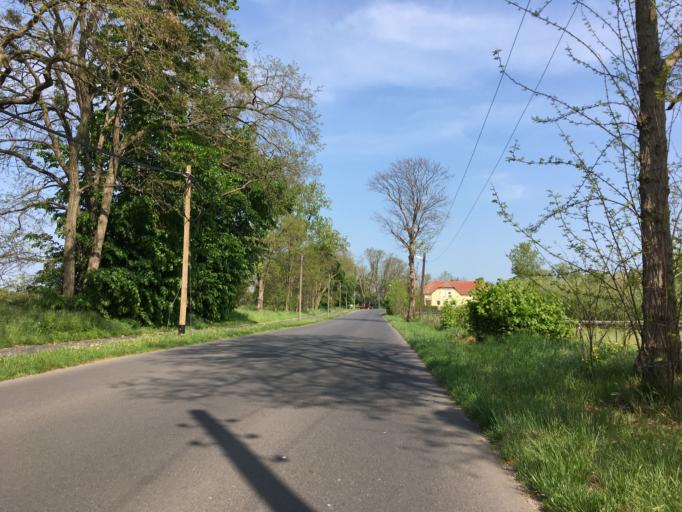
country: DE
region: Brandenburg
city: Altlandsberg
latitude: 52.5762
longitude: 13.7262
